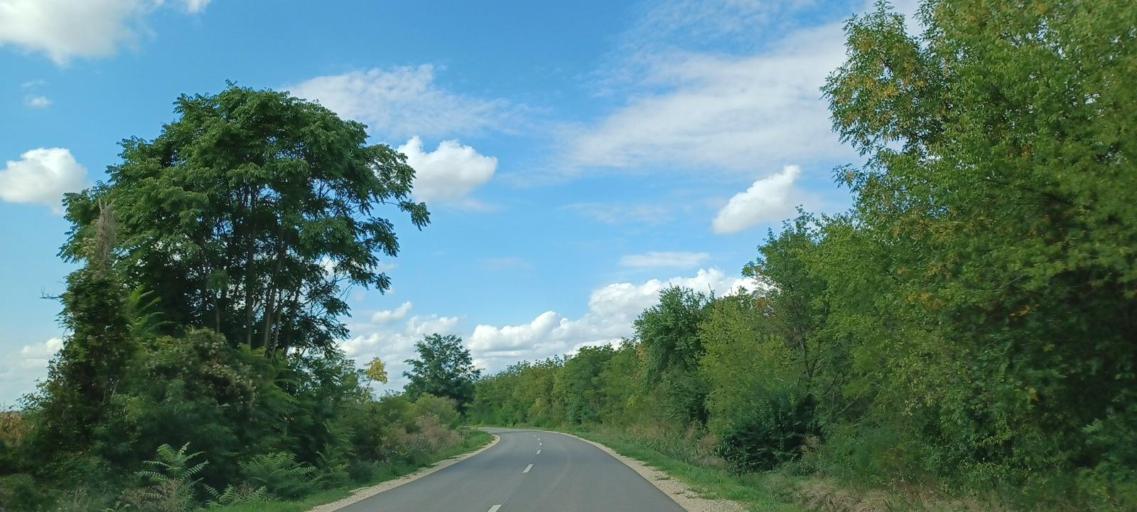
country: HU
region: Tolna
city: Zomba
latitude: 46.4417
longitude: 18.6077
